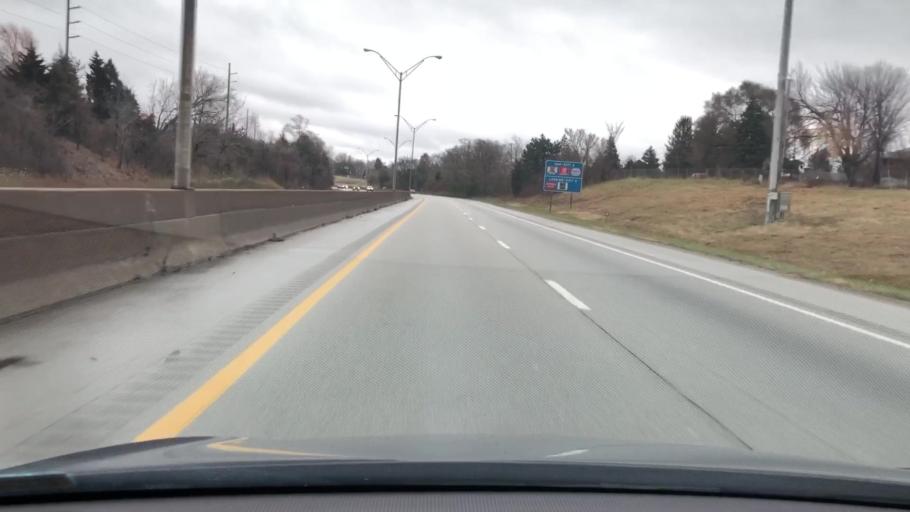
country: US
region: Ohio
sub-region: Lucas County
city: Oregon
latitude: 41.6358
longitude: -83.4907
